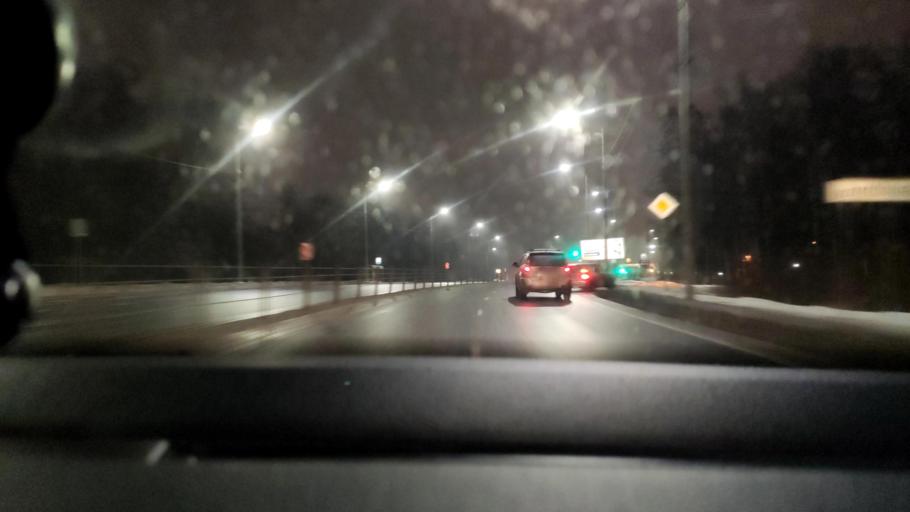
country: RU
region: Moskovskaya
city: Sergiyev Posad
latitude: 56.2690
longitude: 38.1211
